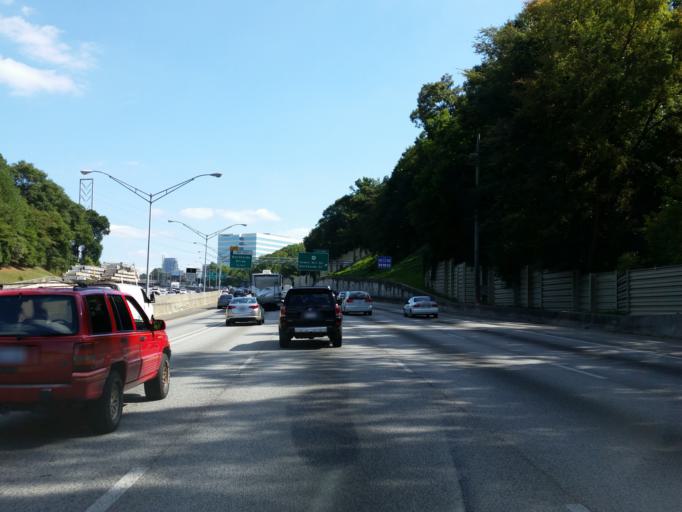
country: US
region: Georgia
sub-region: Fulton County
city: Atlanta
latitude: 33.8092
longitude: -84.4182
